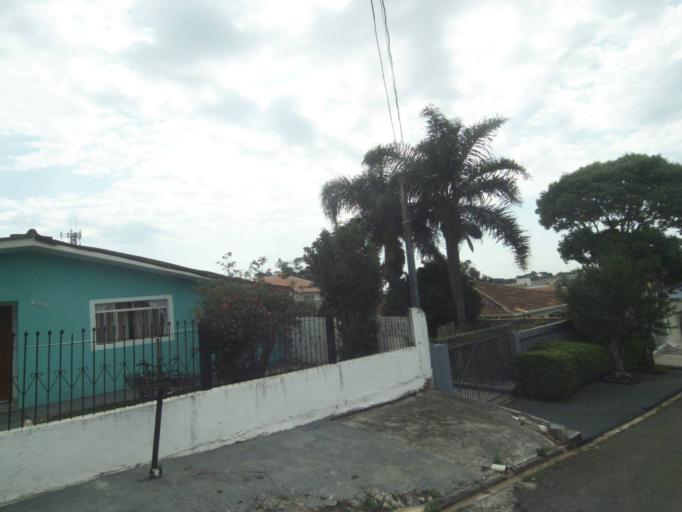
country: BR
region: Parana
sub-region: Sao Jose Dos Pinhais
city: Sao Jose dos Pinhais
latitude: -25.5248
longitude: -49.2592
